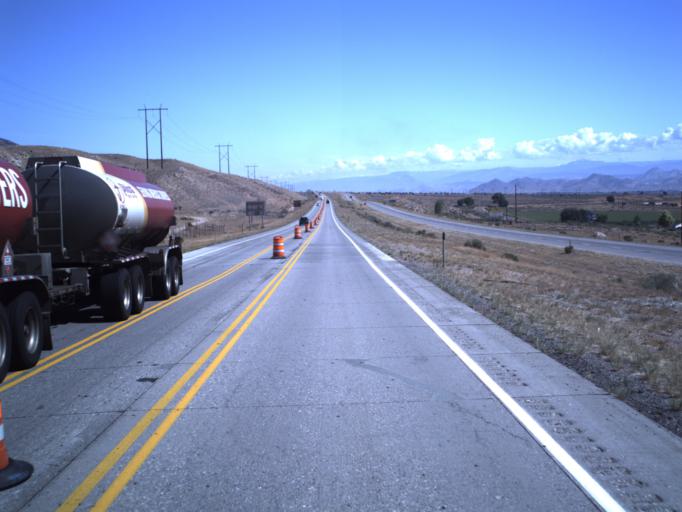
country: US
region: Utah
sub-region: Sevier County
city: Richfield
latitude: 38.7956
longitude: -112.0746
